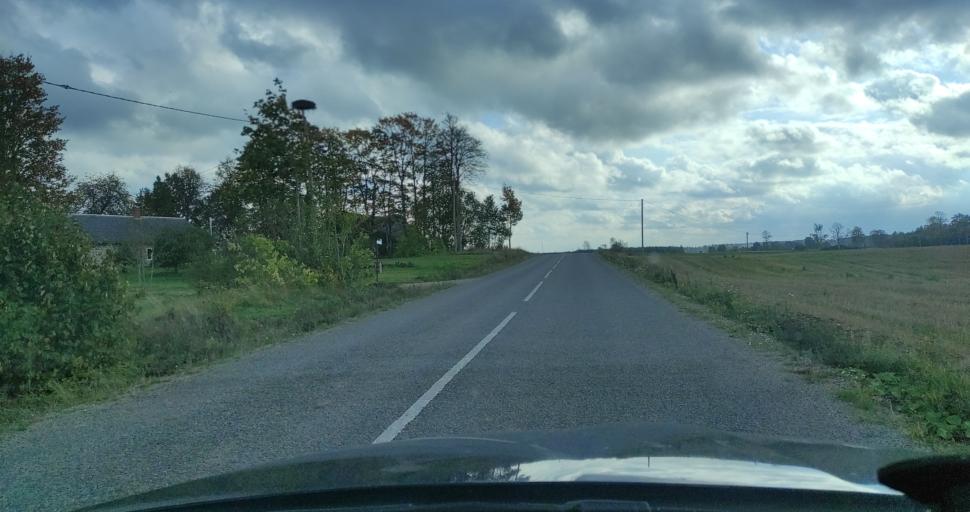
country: LV
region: Talsu Rajons
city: Sabile
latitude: 56.9361
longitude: 22.3967
